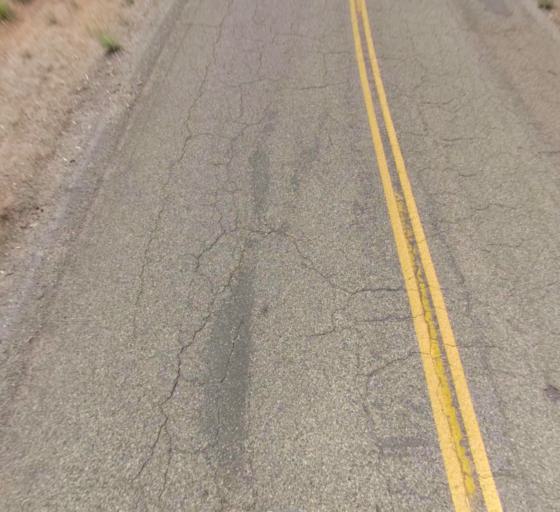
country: US
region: California
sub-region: Fresno County
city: Auberry
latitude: 37.2501
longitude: -119.3471
